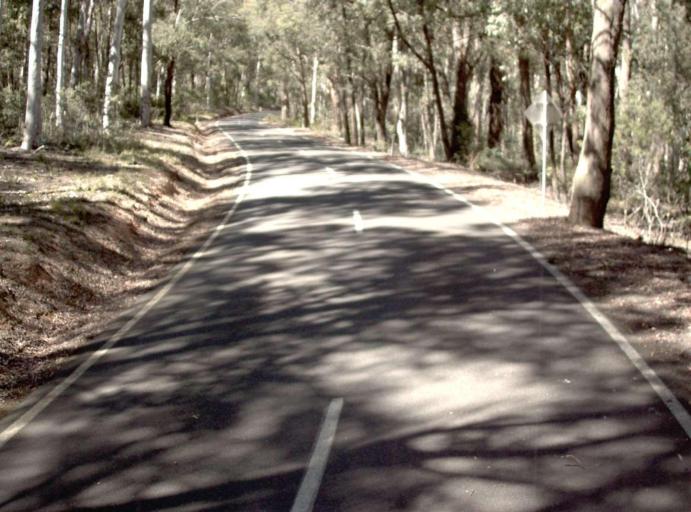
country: AU
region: New South Wales
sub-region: Bombala
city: Bombala
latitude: -37.1255
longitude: 148.7485
